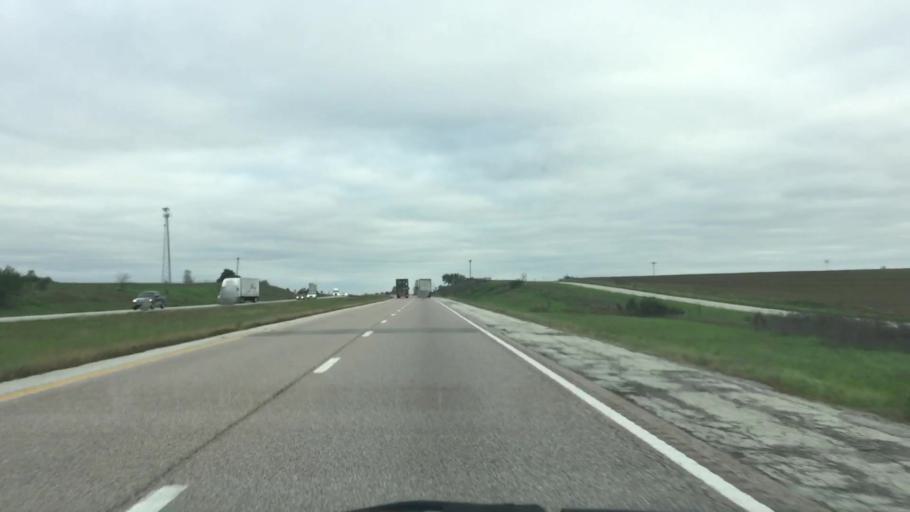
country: US
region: Missouri
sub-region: Clinton County
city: Lathrop
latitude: 39.5689
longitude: -94.2628
